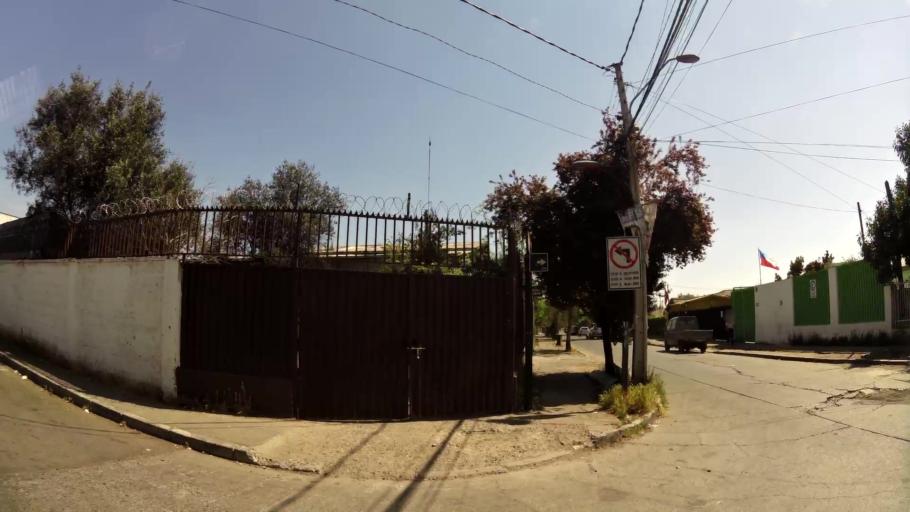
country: CL
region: Santiago Metropolitan
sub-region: Provincia de Santiago
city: La Pintana
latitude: -33.5320
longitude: -70.6365
